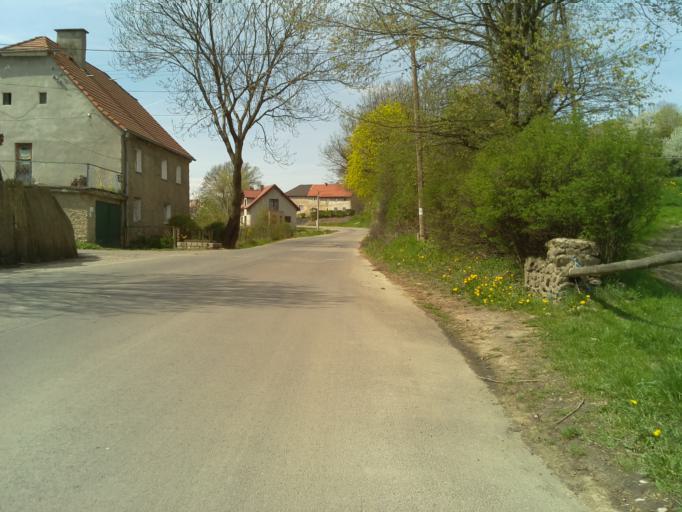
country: PL
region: Lower Silesian Voivodeship
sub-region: Powiat swidnicki
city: Swiebodzice
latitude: 50.8314
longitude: 16.3300
